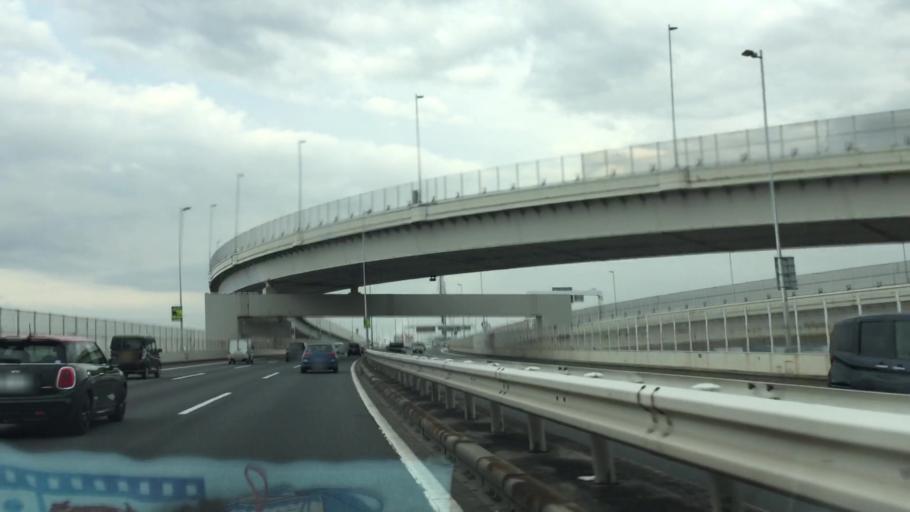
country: JP
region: Kanagawa
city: Yokohama
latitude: 35.4644
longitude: 139.6823
